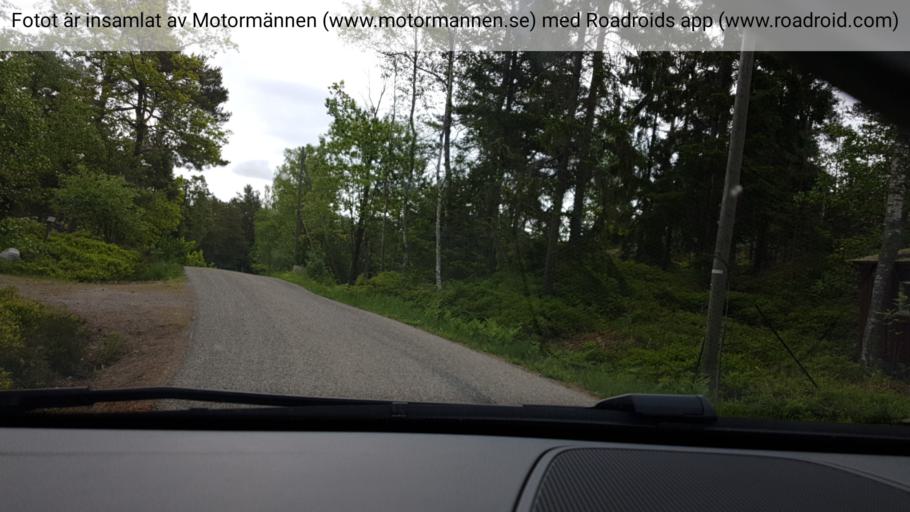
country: SE
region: Stockholm
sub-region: Haninge Kommun
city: Jordbro
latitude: 59.0171
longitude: 18.1052
